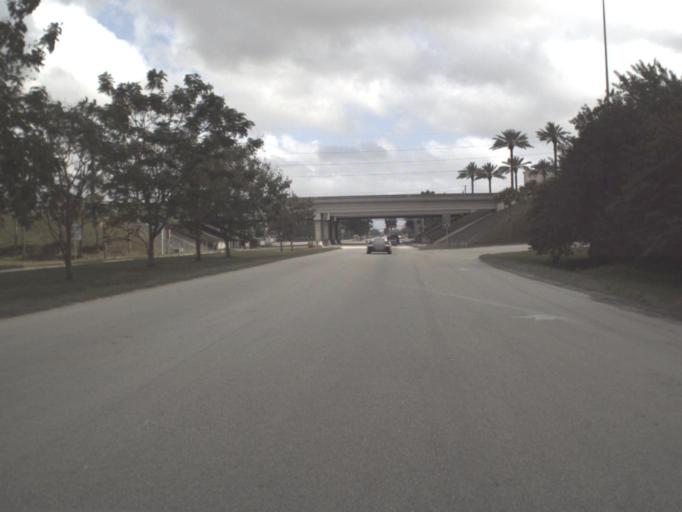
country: US
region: Florida
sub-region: Miami-Dade County
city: Doral
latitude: 25.8117
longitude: -80.3883
